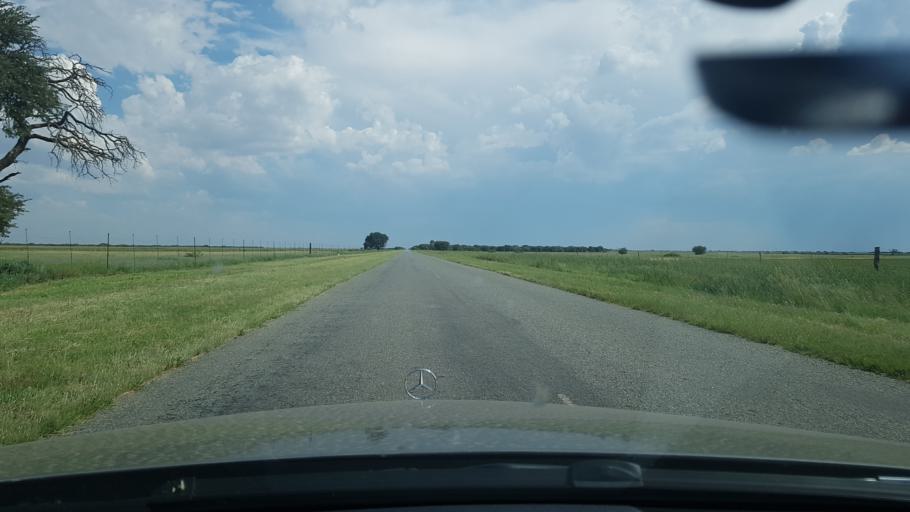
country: ZA
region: North-West
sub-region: Dr Ruth Segomotsi Mompati District Municipality
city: Bloemhof
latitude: -27.6817
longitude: 25.5883
